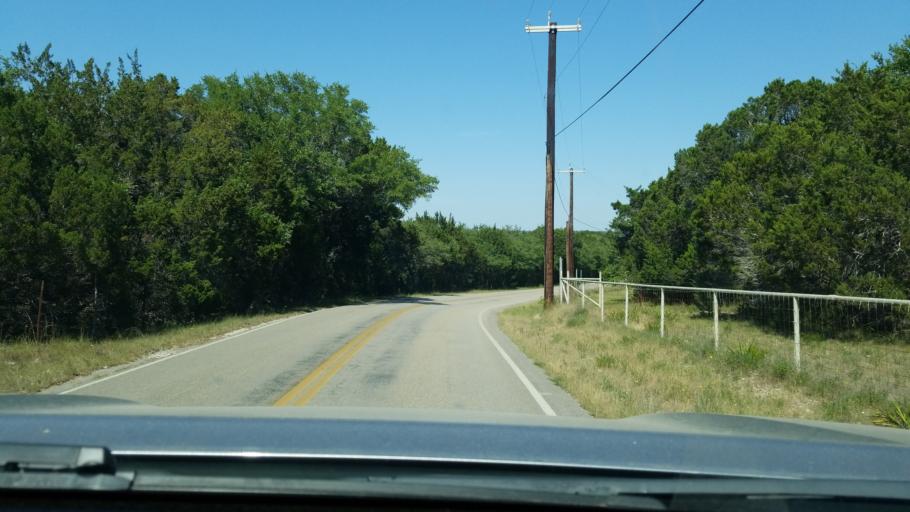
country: US
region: Texas
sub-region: Comal County
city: Bulverde
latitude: 29.7595
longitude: -98.4868
